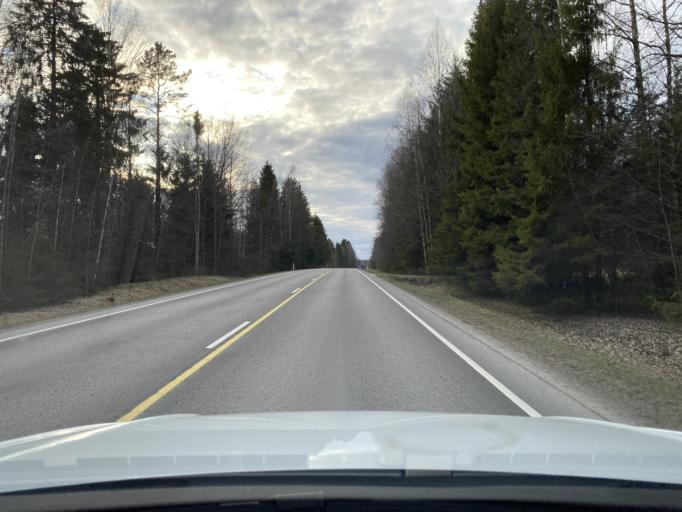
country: FI
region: Haeme
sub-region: Haemeenlinna
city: Renko
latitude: 60.7914
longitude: 24.1182
